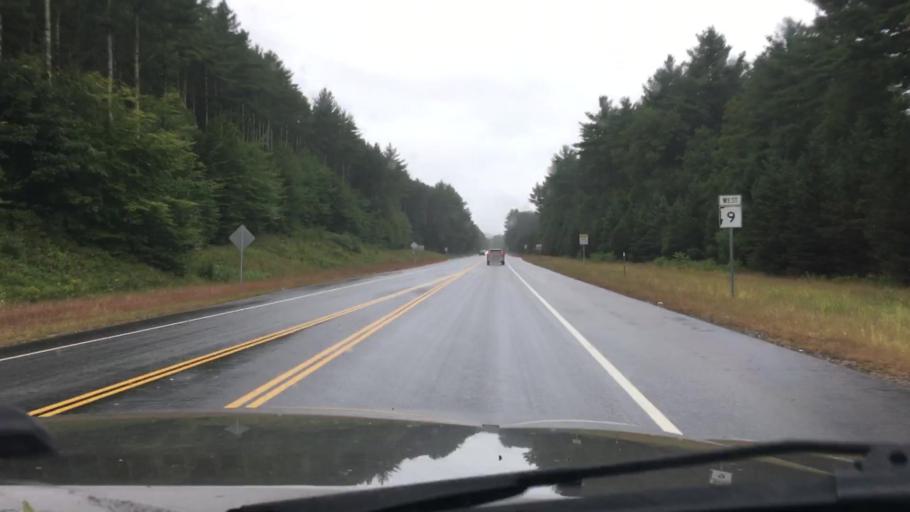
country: US
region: New Hampshire
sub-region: Cheshire County
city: Keene
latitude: 42.9256
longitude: -72.3142
